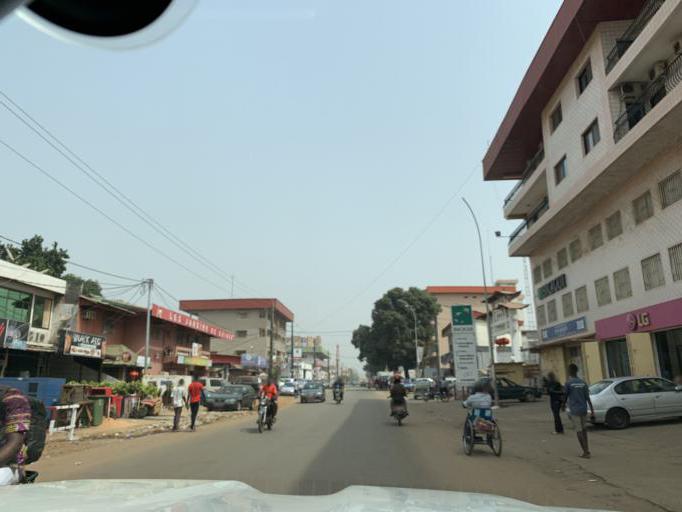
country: GN
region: Conakry
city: Camayenne
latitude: 9.5289
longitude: -13.6829
